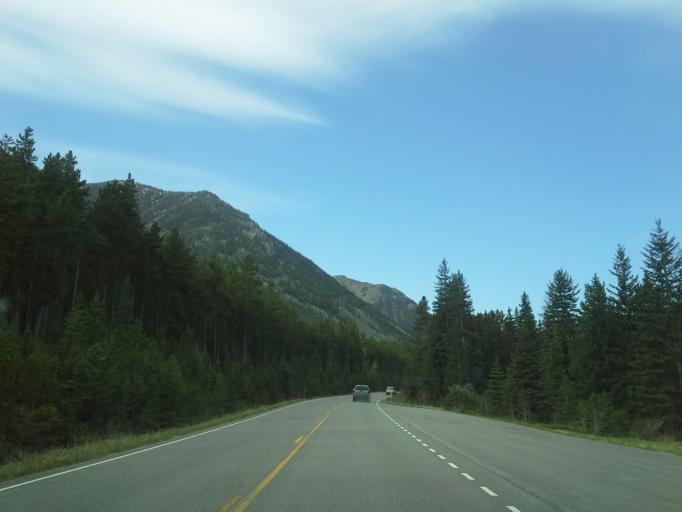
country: US
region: Montana
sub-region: Carbon County
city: Red Lodge
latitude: 45.0718
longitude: -109.3868
